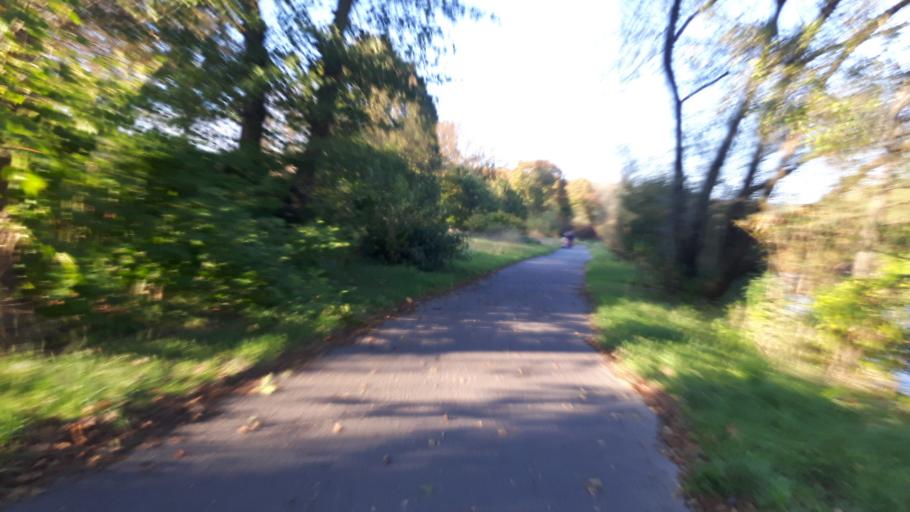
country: DE
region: North Rhine-Westphalia
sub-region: Regierungsbezirk Koln
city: Ruppichteroth
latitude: 50.8025
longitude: 7.5385
